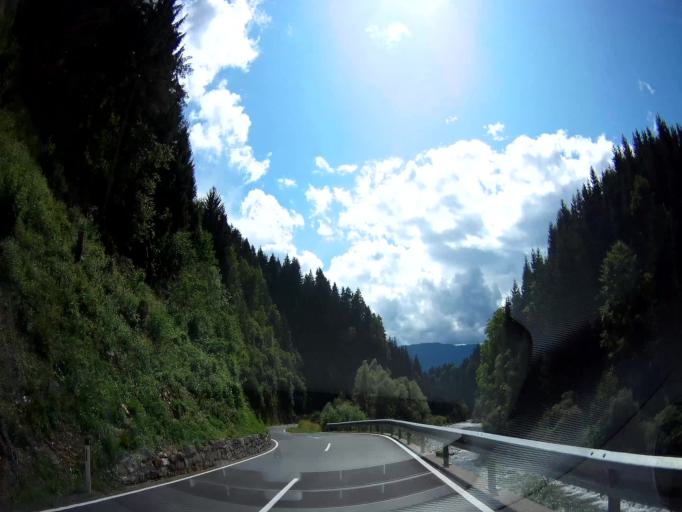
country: AT
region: Carinthia
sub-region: Politischer Bezirk Spittal an der Drau
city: Seeboden
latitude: 46.8482
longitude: 13.5036
